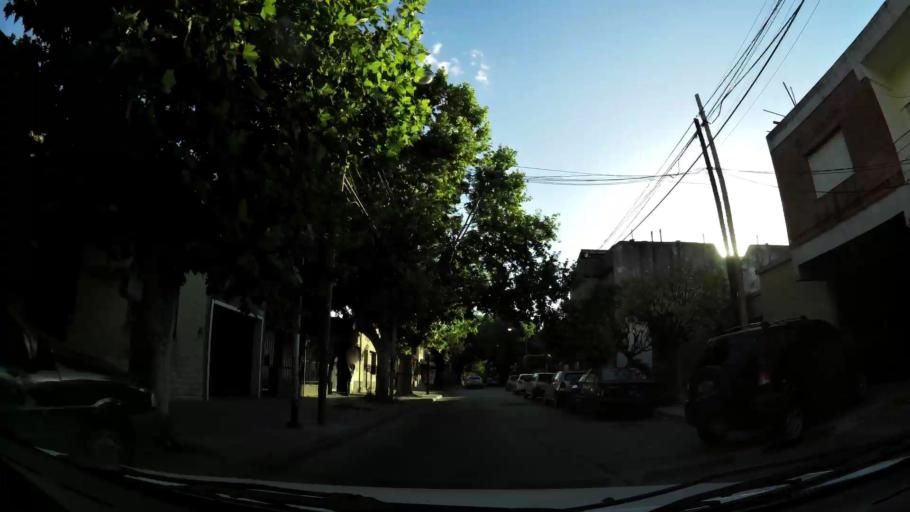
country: AR
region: Buenos Aires
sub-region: Partido de General San Martin
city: General San Martin
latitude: -34.5697
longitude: -58.5486
